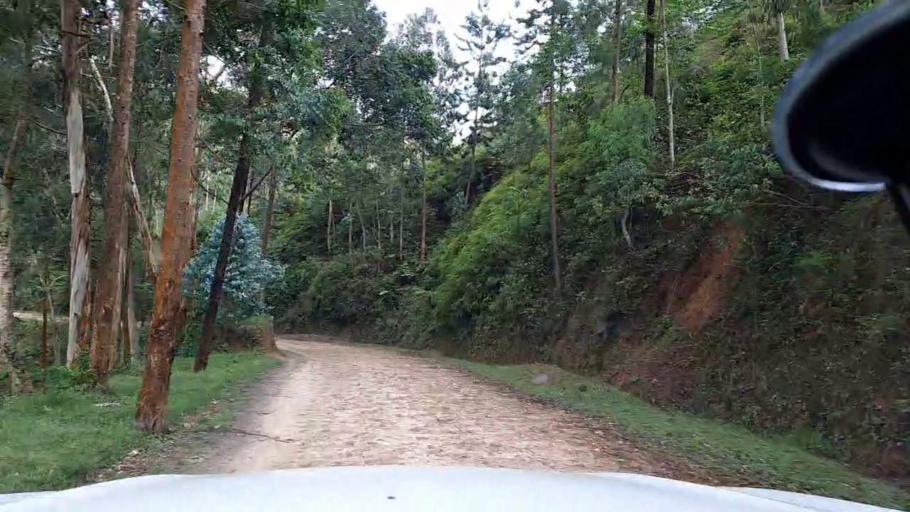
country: RW
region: Southern Province
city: Gitarama
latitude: -2.1638
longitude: 29.5497
